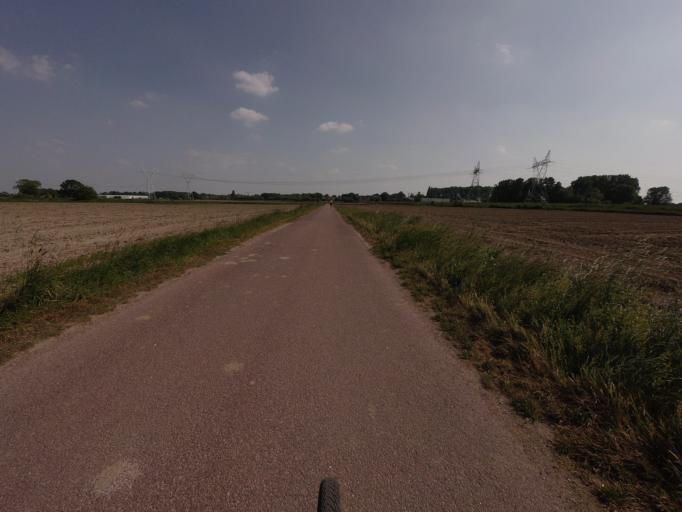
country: BE
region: Flanders
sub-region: Provincie Antwerpen
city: Borsbeek
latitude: 51.1783
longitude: 4.4748
